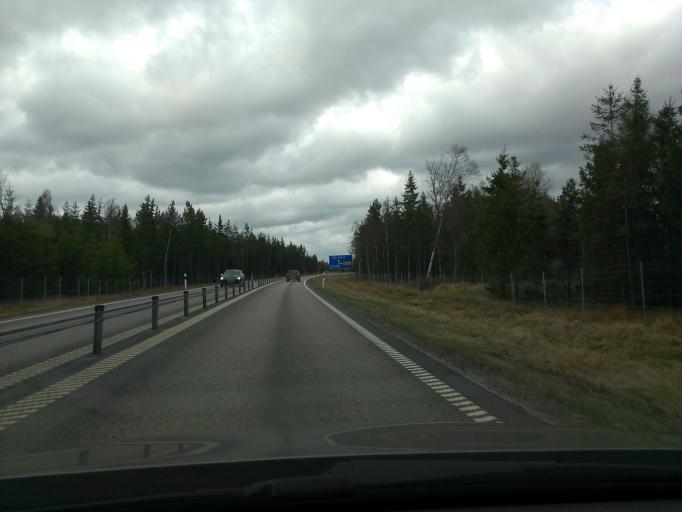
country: SE
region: Kronoberg
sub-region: Alvesta Kommun
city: Vislanda
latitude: 56.6821
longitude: 14.3172
